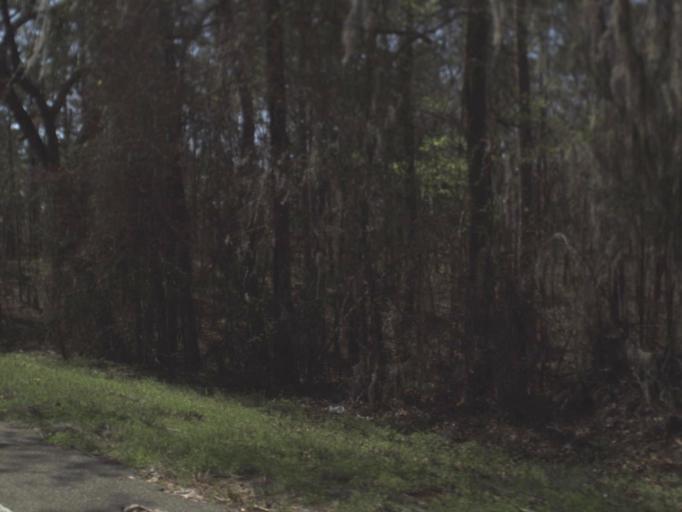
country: US
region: Florida
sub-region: Jefferson County
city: Monticello
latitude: 30.3877
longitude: -84.0102
